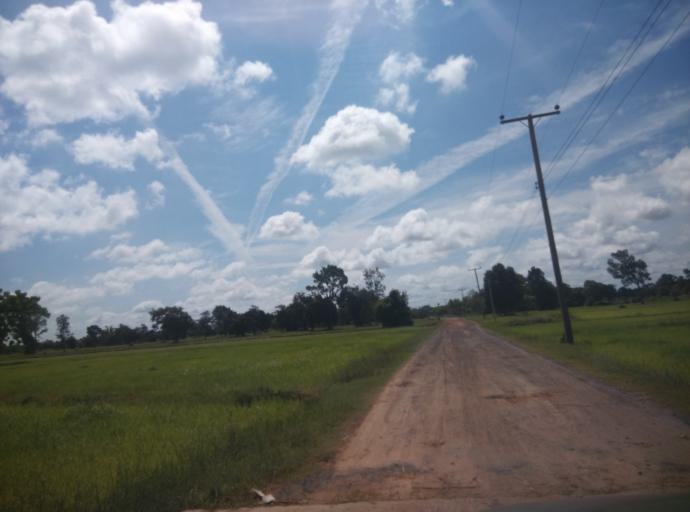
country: TH
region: Sisaket
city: Prang Ku
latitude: 14.9457
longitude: 104.0697
